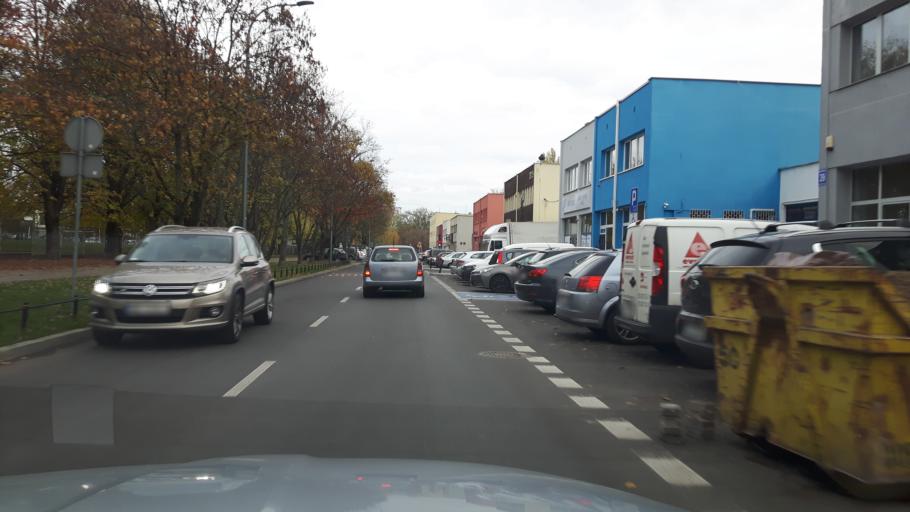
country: PL
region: Masovian Voivodeship
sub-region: Warszawa
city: Mokotow
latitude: 52.1680
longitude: 21.0045
